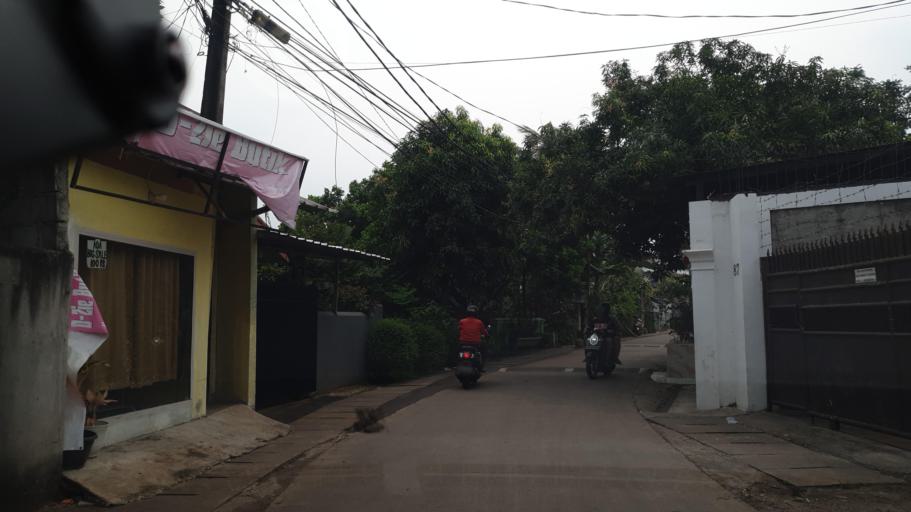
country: ID
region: West Java
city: Pamulang
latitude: -6.3306
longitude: 106.7734
